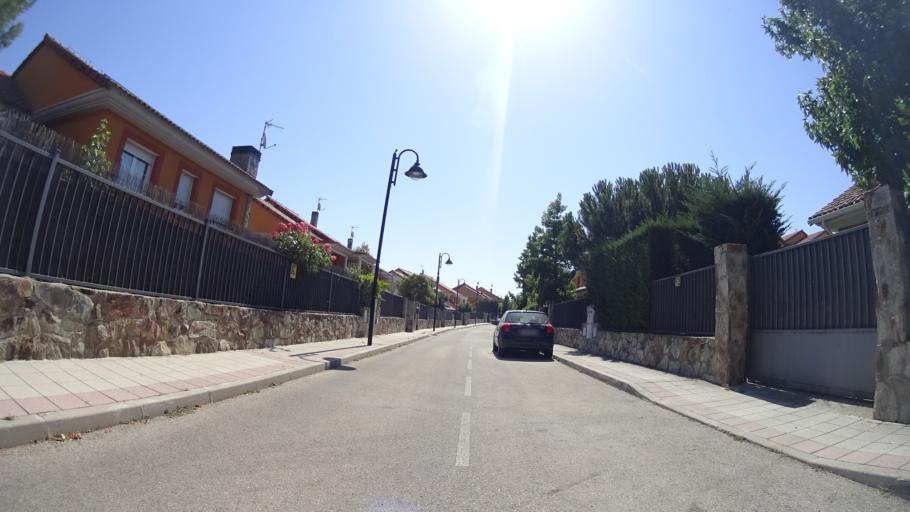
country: ES
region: Madrid
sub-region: Provincia de Madrid
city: Galapagar
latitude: 40.5959
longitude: -3.9818
